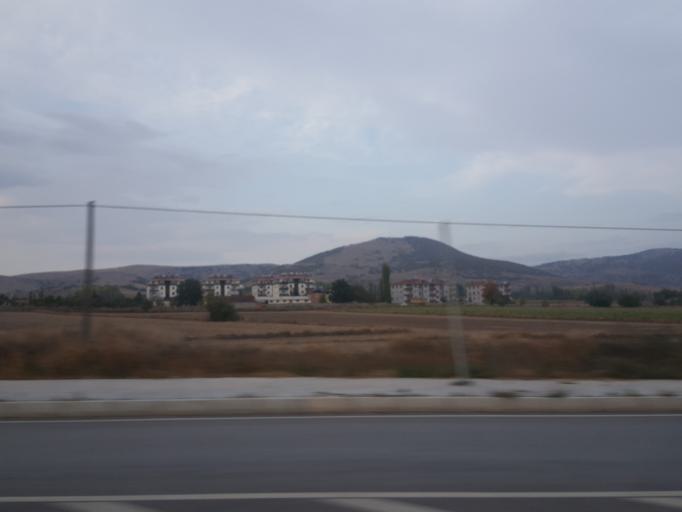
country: TR
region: Amasya
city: Gumushacikoy
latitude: 40.8839
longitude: 35.2140
